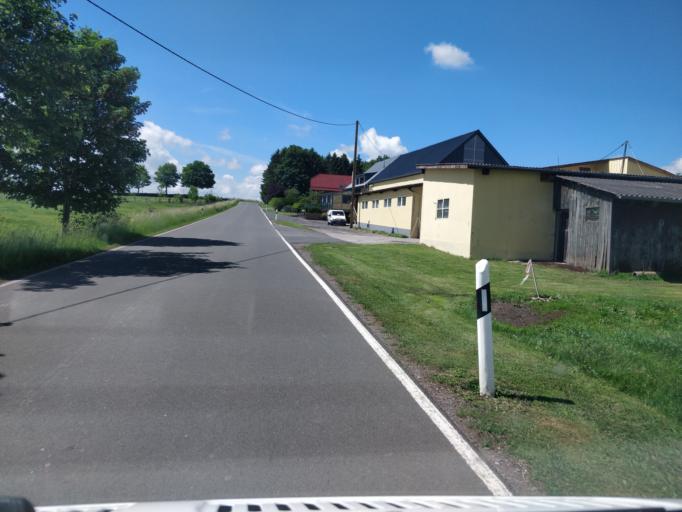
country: DE
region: Rheinland-Pfalz
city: Scheid
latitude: 50.3645
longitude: 6.4220
